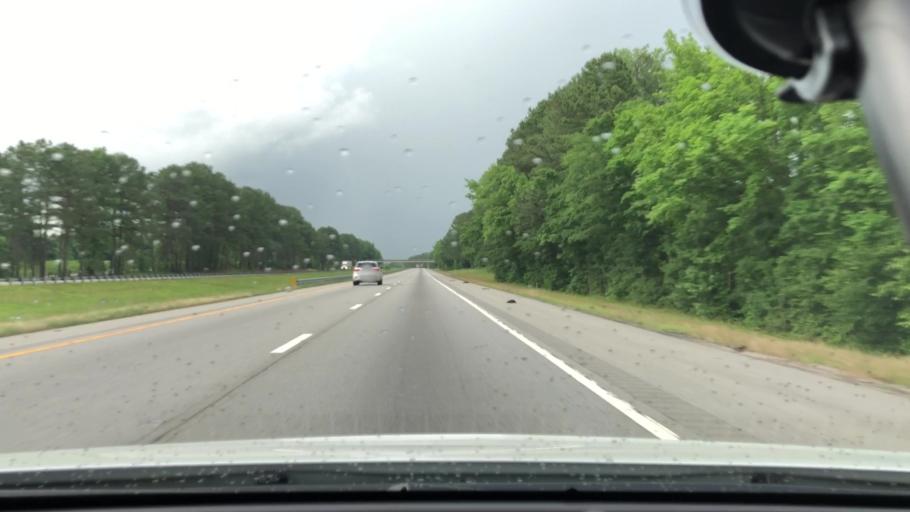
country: US
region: North Carolina
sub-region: Halifax County
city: Enfield
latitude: 36.2862
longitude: -77.7158
